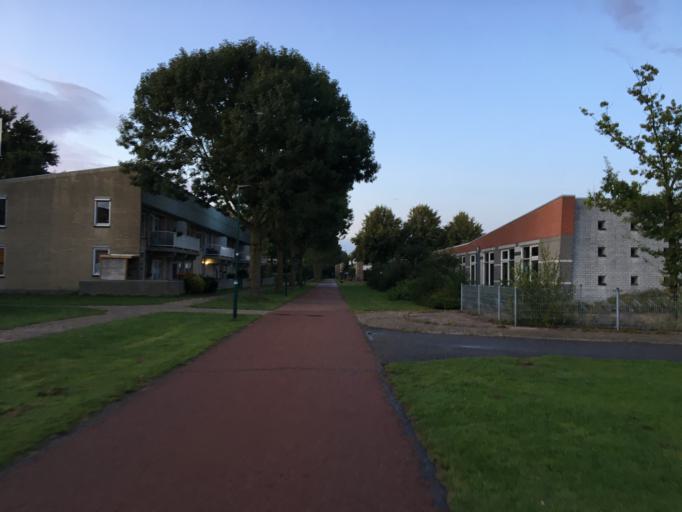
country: NL
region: Utrecht
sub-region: Gemeente Houten
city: Houten
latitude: 52.0287
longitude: 5.1526
